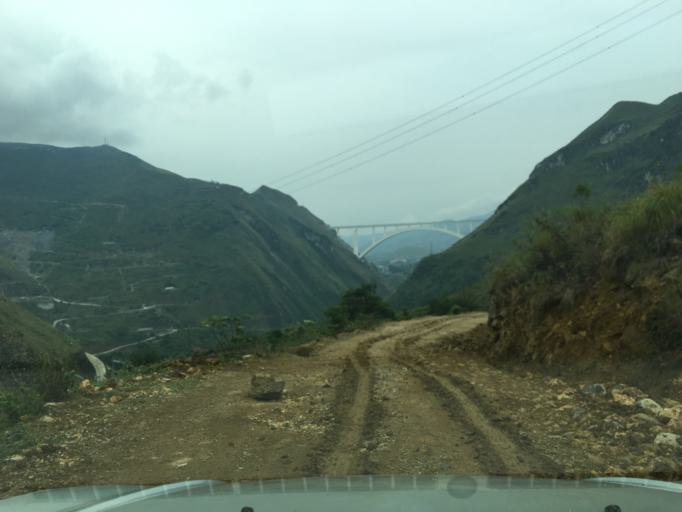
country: CN
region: Guizhou Sheng
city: Anshun
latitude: 25.9635
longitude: 105.2413
